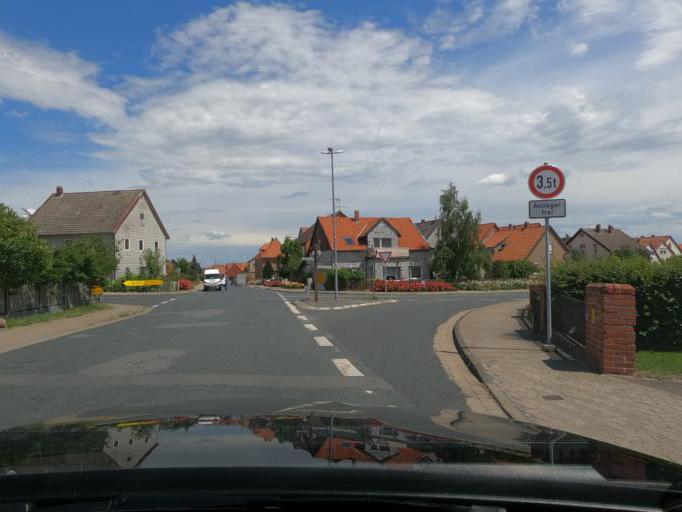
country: DE
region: Lower Saxony
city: Sohlde
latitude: 52.1902
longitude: 10.2292
